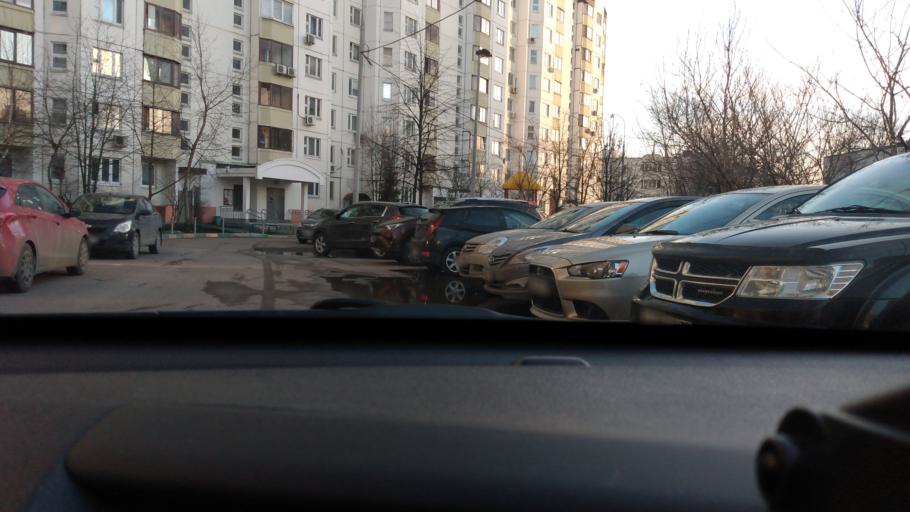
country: RU
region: Moscow
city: Annino
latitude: 55.5489
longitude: 37.5660
